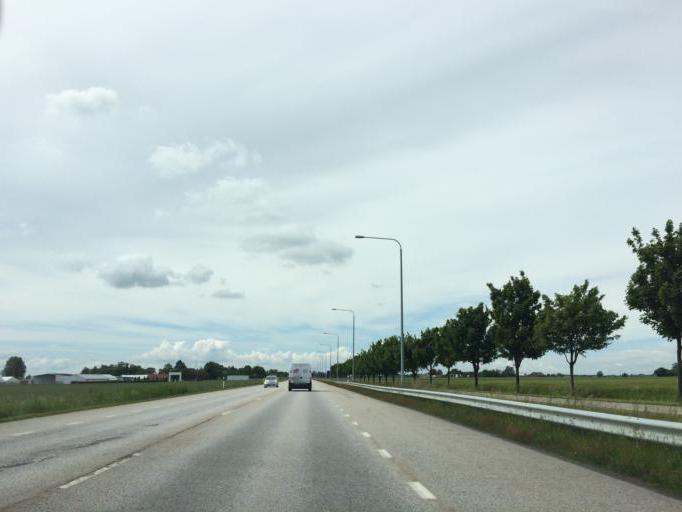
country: SE
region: Skane
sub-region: Staffanstorps Kommun
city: Hjaerup
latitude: 55.7217
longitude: 13.1397
